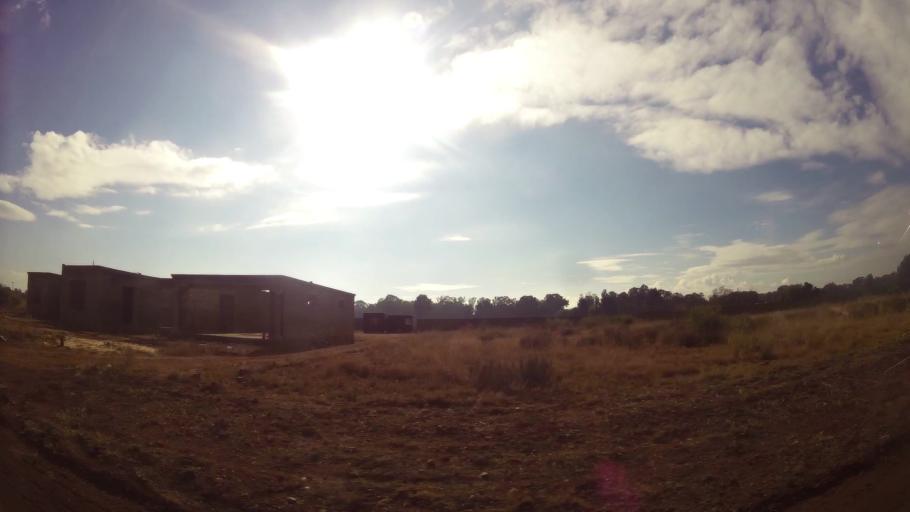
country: ZA
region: Gauteng
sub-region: Sedibeng District Municipality
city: Meyerton
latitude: -26.5479
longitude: 28.0496
